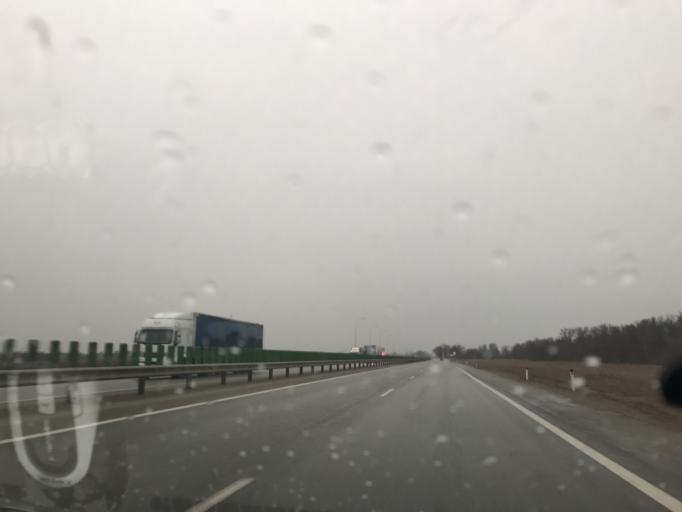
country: RU
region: Krasnodarskiy
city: Pavlovskaya
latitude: 46.2724
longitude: 39.8317
